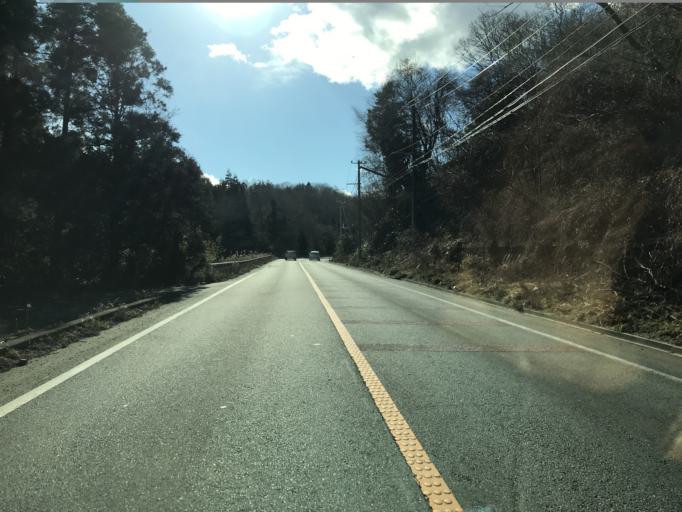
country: JP
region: Fukushima
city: Iwaki
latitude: 37.1125
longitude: 140.8971
